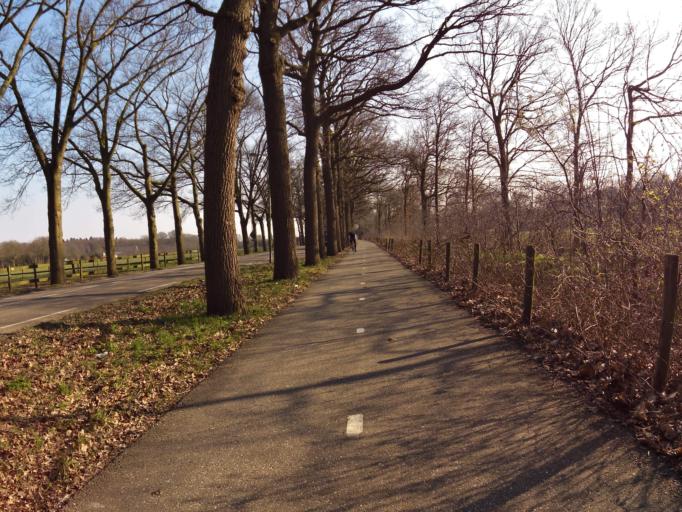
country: NL
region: North Brabant
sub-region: Gemeente Maasdonk
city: Geffen
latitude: 51.7192
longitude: 5.4006
